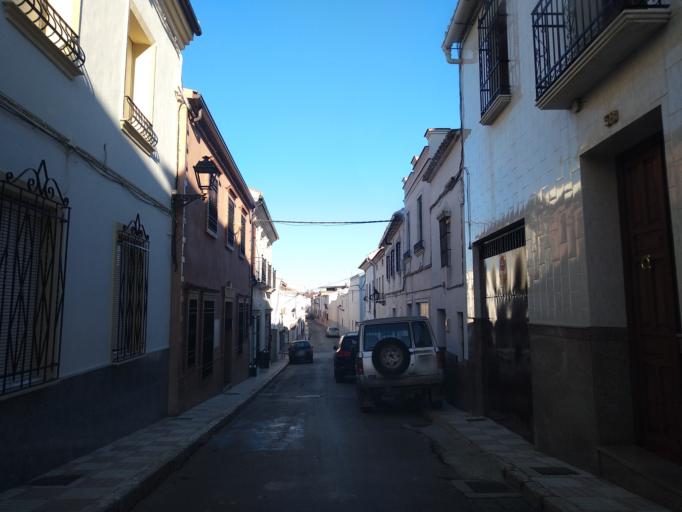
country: ES
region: Andalusia
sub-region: Provincia de Malaga
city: Campillos
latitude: 37.0496
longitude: -4.8645
